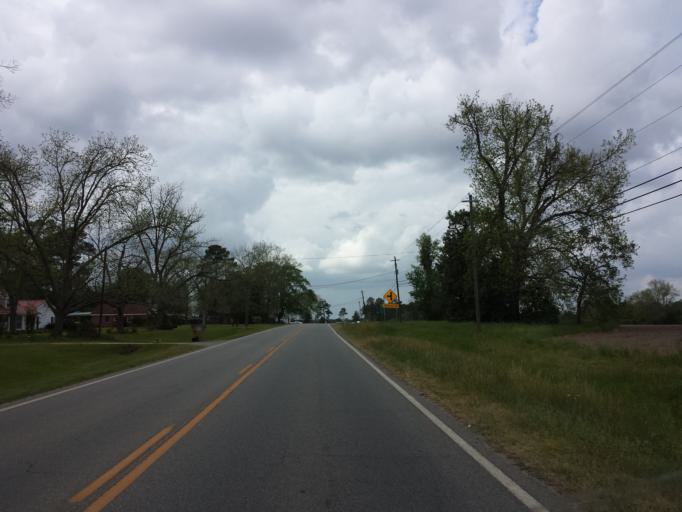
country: US
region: Georgia
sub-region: Cook County
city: Sparks
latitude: 31.1800
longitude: -83.4419
